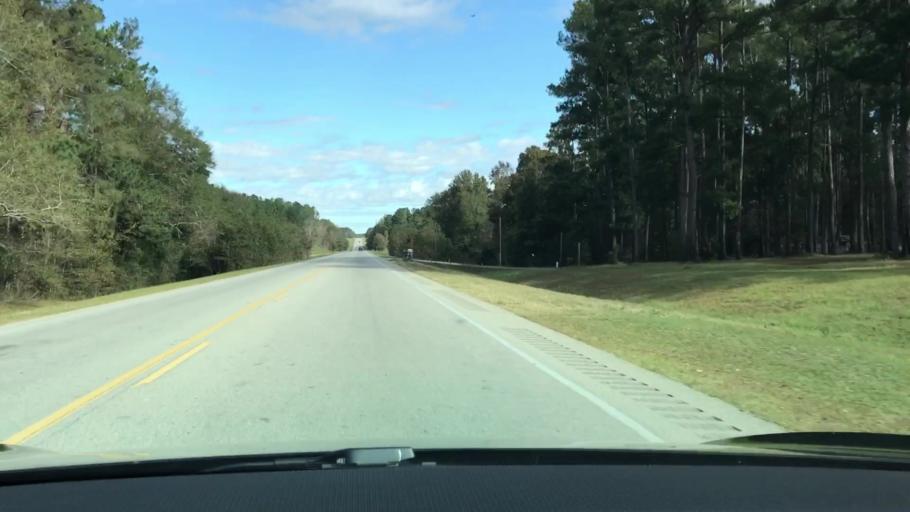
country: US
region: Georgia
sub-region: Jefferson County
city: Louisville
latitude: 32.9354
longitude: -82.3962
